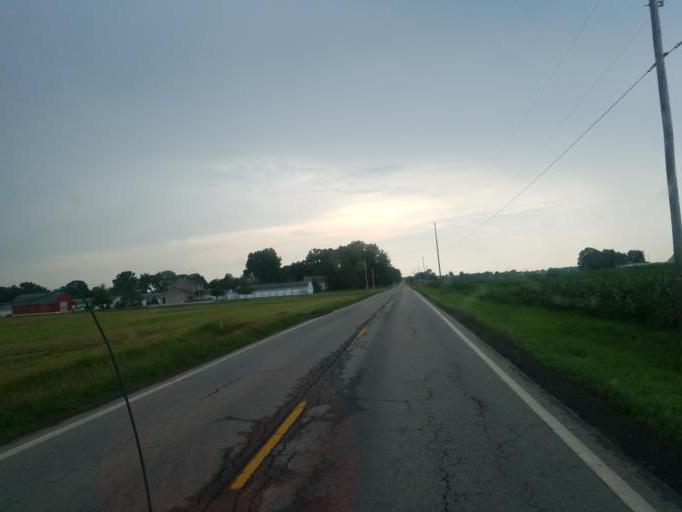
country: US
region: Ohio
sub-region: Wayne County
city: Rittman
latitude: 40.9460
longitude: -81.7896
